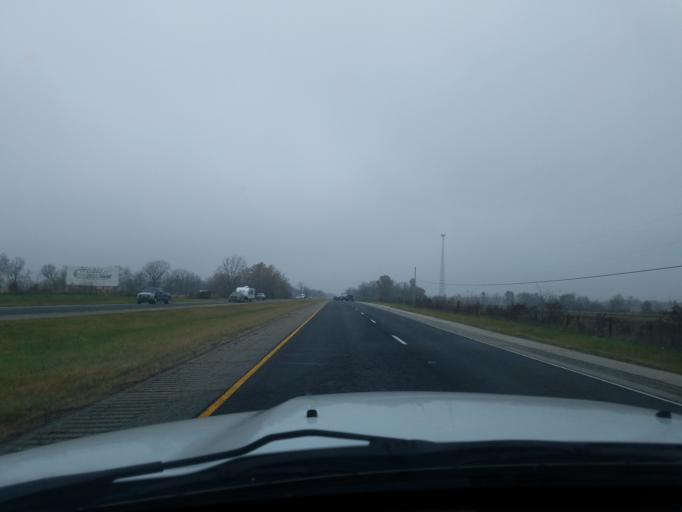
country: US
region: Indiana
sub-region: Hamilton County
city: Westfield
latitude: 40.1177
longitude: -86.1279
